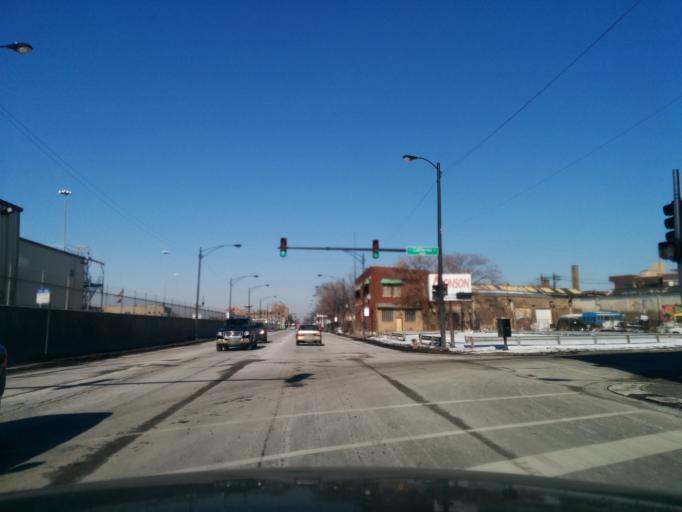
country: US
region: Illinois
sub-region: Cook County
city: Chicago
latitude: 41.8942
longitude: -87.6964
